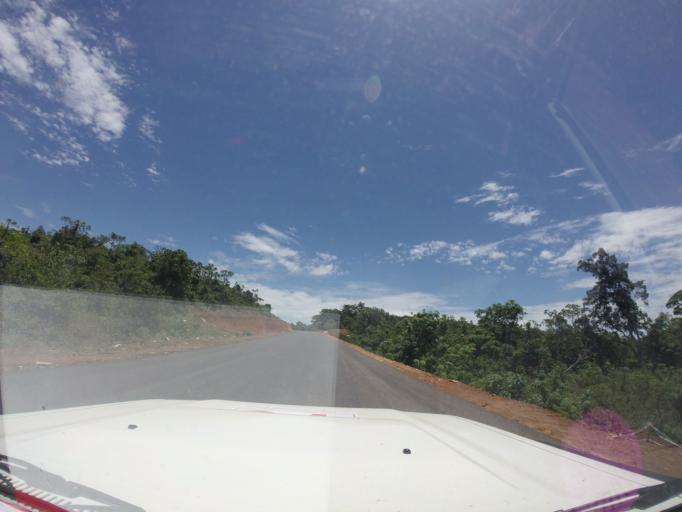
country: LR
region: Margibi
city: Kakata
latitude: 6.7770
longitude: -9.9936
